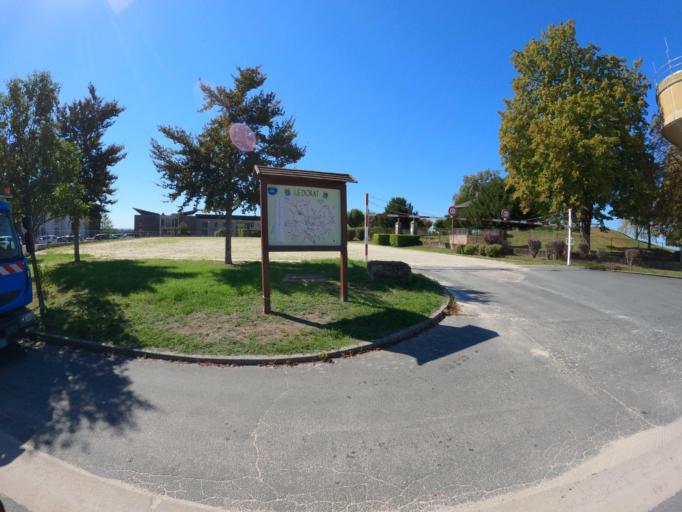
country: FR
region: Limousin
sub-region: Departement de la Haute-Vienne
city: Le Dorat
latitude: 46.2183
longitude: 1.0772
